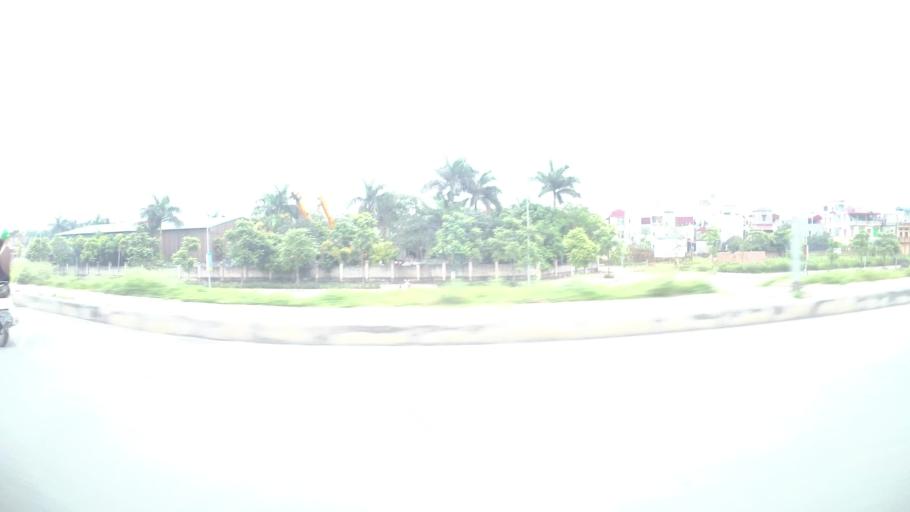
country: VN
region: Ha Noi
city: Trau Quy
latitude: 21.0771
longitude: 105.9039
